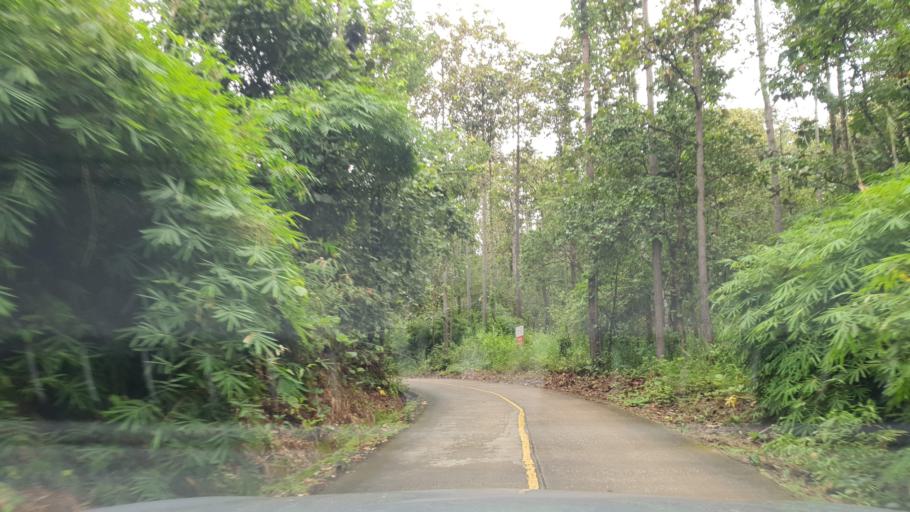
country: TH
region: Chiang Mai
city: Mae Taeng
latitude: 19.2152
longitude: 98.9277
